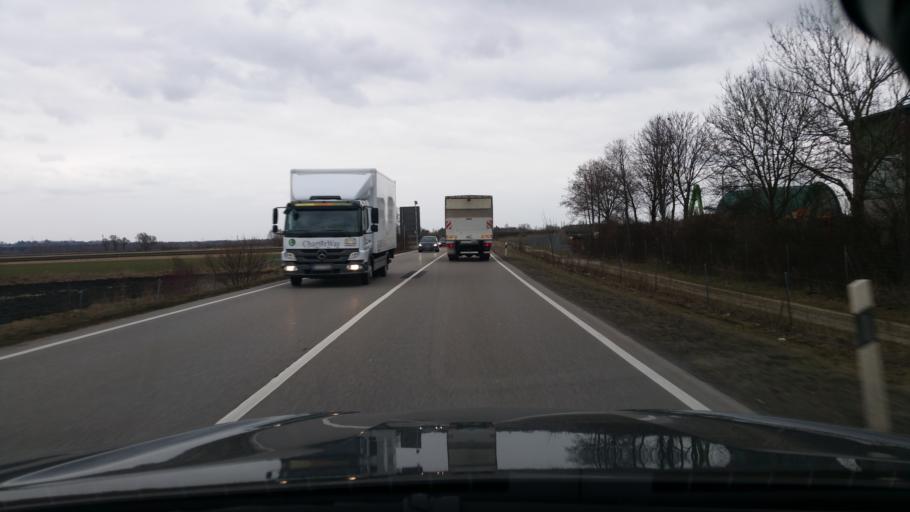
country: DE
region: Bavaria
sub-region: Upper Bavaria
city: Eitting
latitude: 48.3731
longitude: 11.8555
